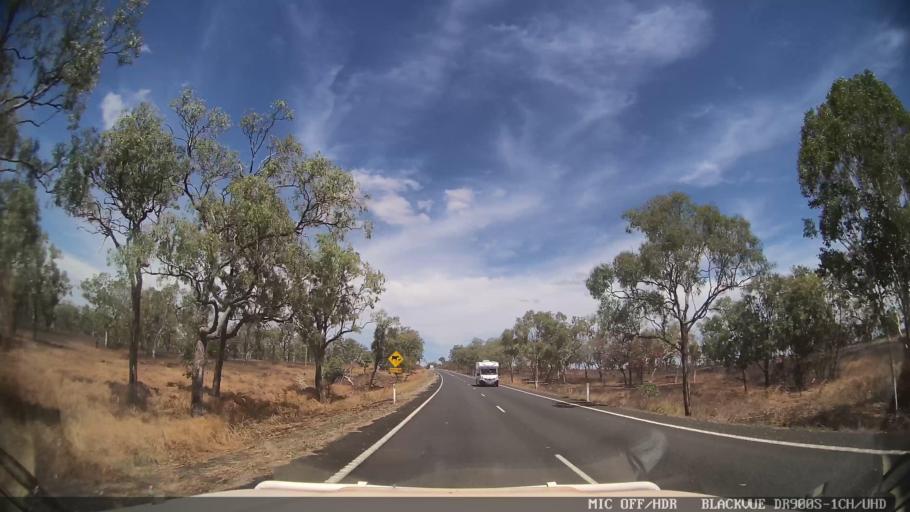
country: AU
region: Queensland
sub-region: Cook
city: Cooktown
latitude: -15.8017
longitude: 144.9226
